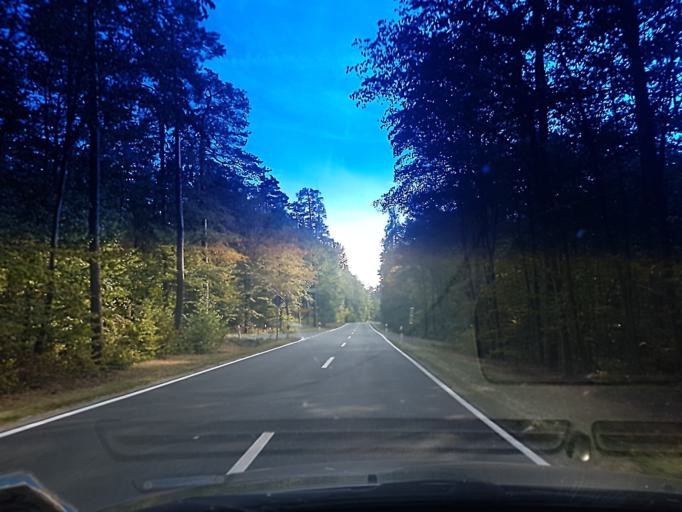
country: DE
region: Bavaria
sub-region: Upper Franconia
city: Burgwindheim
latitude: 49.7924
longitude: 10.5715
